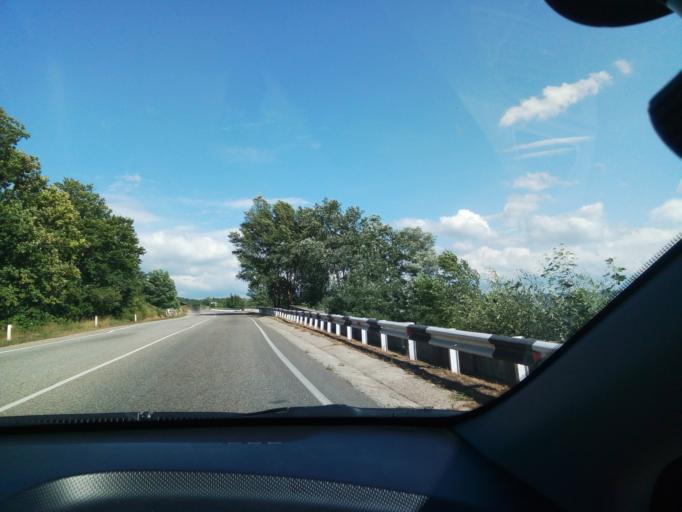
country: RU
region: Krasnodarskiy
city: Khadyzhensk
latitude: 44.4140
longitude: 39.5599
